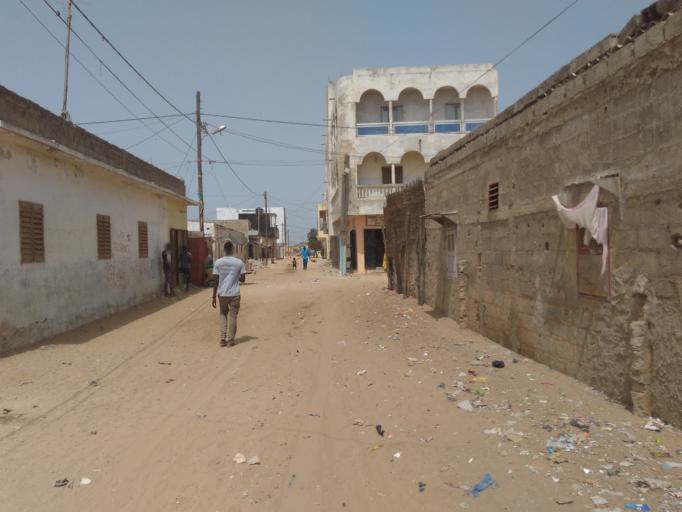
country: SN
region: Dakar
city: Pikine
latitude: 14.7908
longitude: -17.3378
